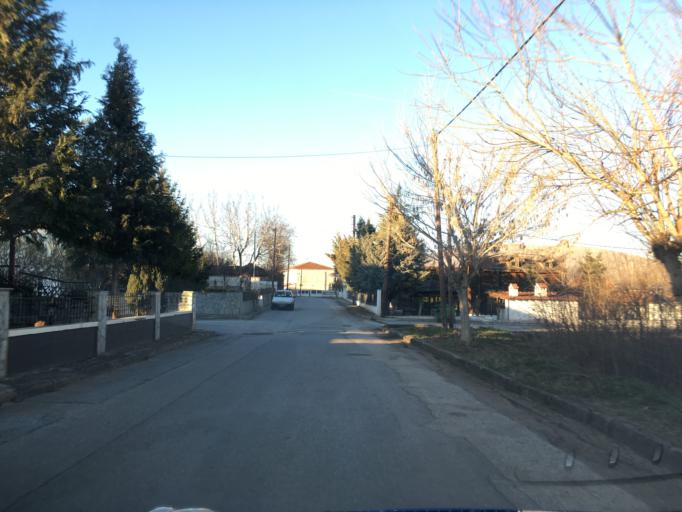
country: GR
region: West Macedonia
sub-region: Nomos Kozanis
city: Kozani
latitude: 40.2843
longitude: 21.7328
